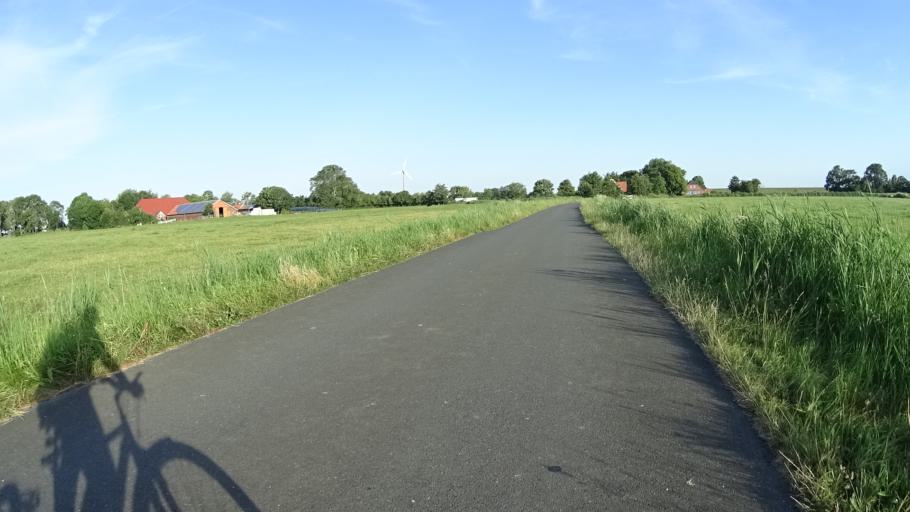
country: DE
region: Lower Saxony
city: Butjadingen
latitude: 53.6012
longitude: 8.2835
